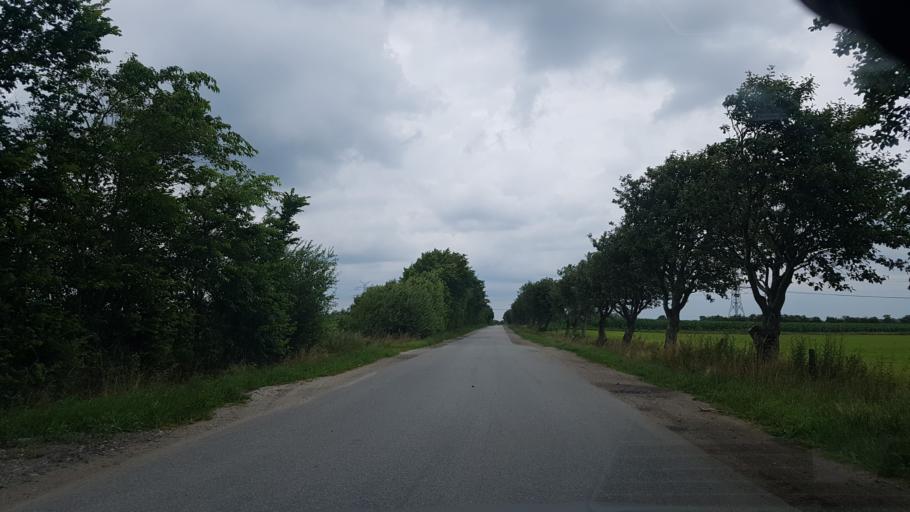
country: DE
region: Schleswig-Holstein
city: Osterby
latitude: 54.7987
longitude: 9.2410
